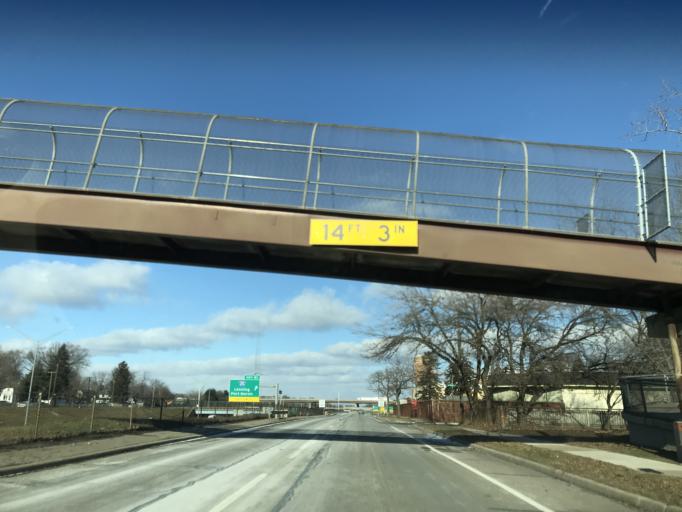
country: US
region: Michigan
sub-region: Oakland County
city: Hazel Park
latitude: 42.4710
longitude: -83.1096
